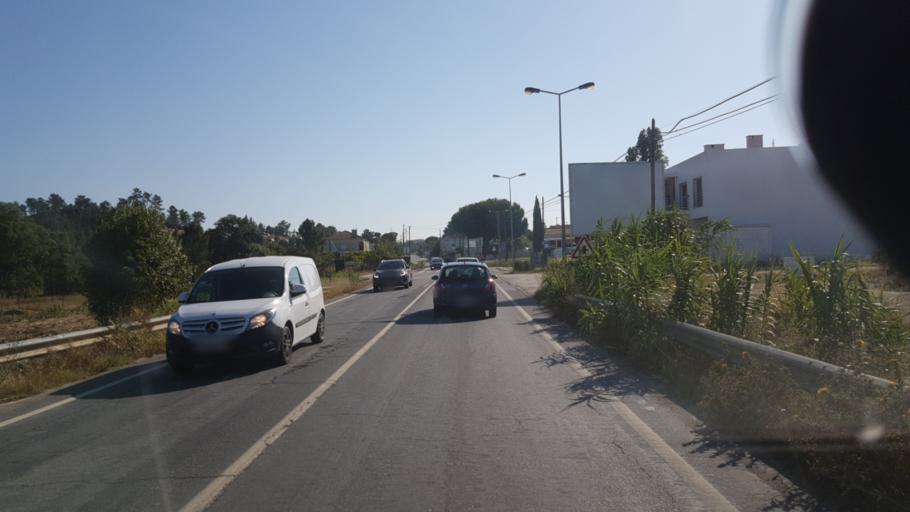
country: PT
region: Setubal
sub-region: Sesimbra
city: Sesimbra
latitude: 38.4750
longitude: -9.0793
